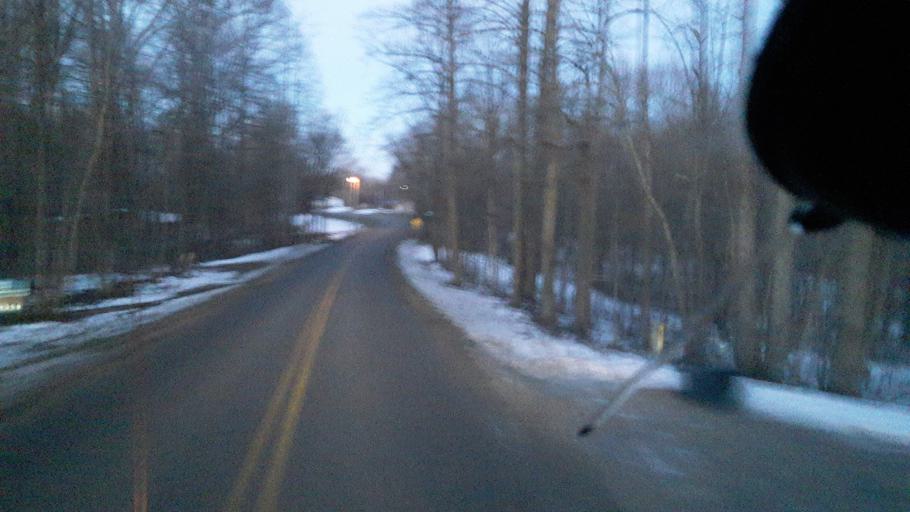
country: US
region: Ohio
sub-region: Perry County
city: New Lexington
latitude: 39.7114
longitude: -82.2473
